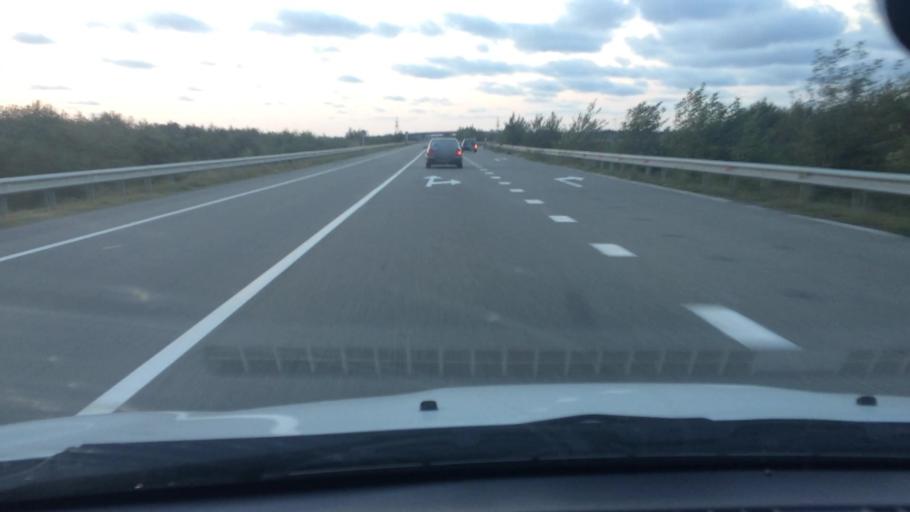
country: GE
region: Ajaria
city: Ochkhamuri
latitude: 41.8939
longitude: 41.8030
